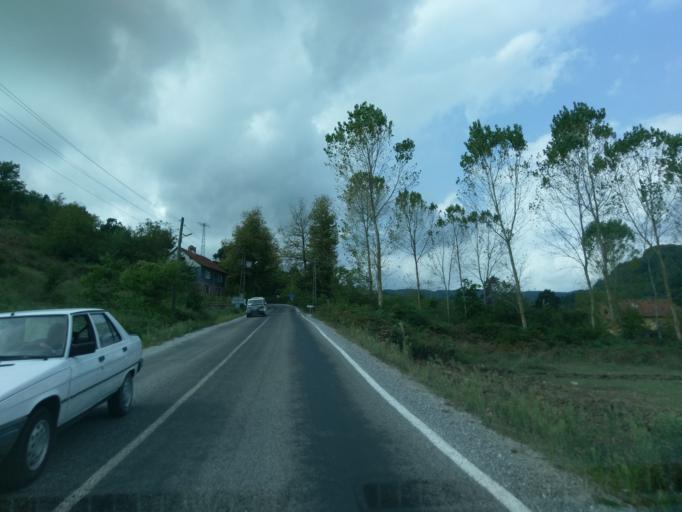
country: TR
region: Sinop
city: Helaldi
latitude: 41.9224
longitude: 34.4141
